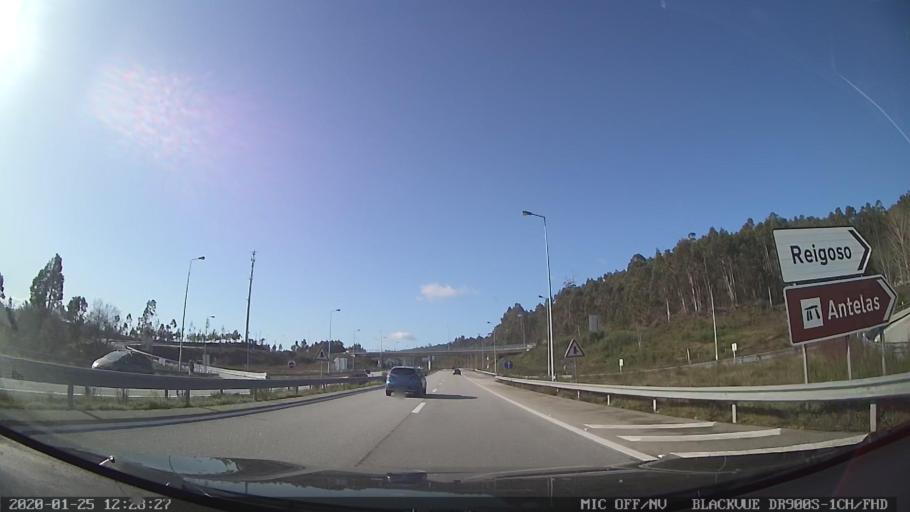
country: PT
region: Viseu
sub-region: Oliveira de Frades
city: Oliveira de Frades
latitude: 40.6881
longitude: -8.2659
